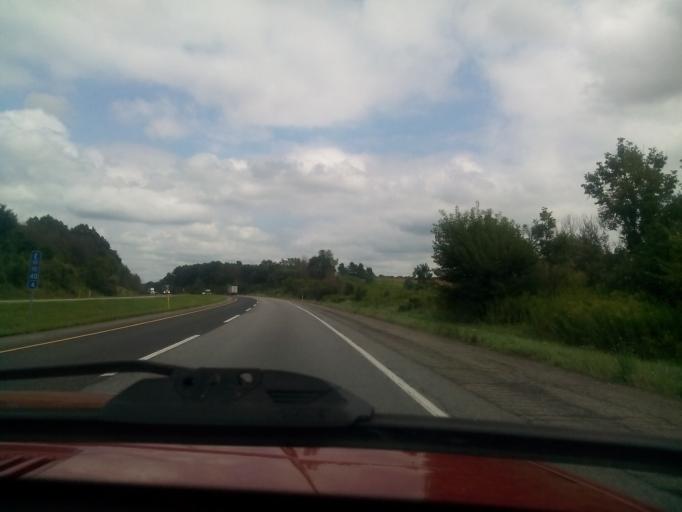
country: US
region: Indiana
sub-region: LaPorte County
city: Westville
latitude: 41.5952
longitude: -86.8714
